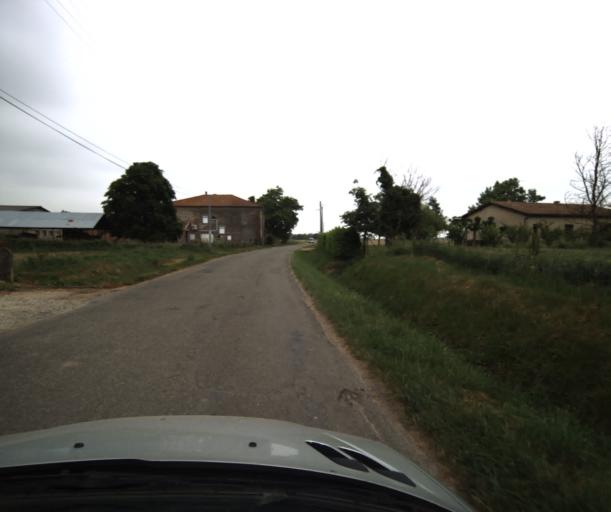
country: FR
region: Midi-Pyrenees
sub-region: Departement du Tarn-et-Garonne
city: Saint-Nicolas-de-la-Grave
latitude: 44.0495
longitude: 1.0186
